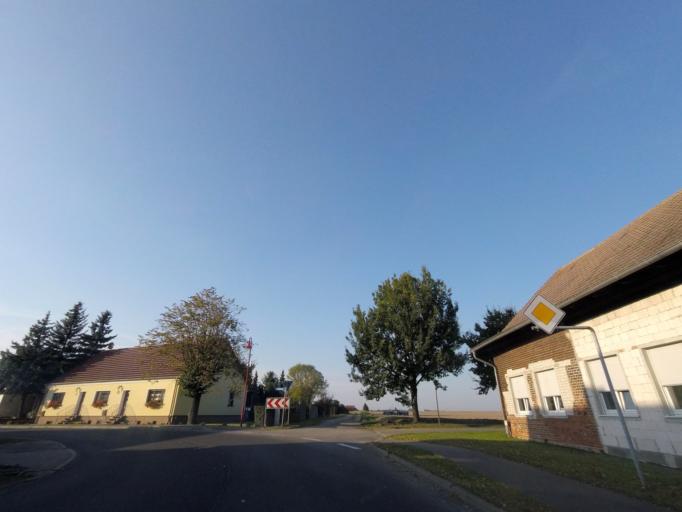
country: DE
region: Saxony-Anhalt
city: Seyda
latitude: 51.9532
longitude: 12.9086
